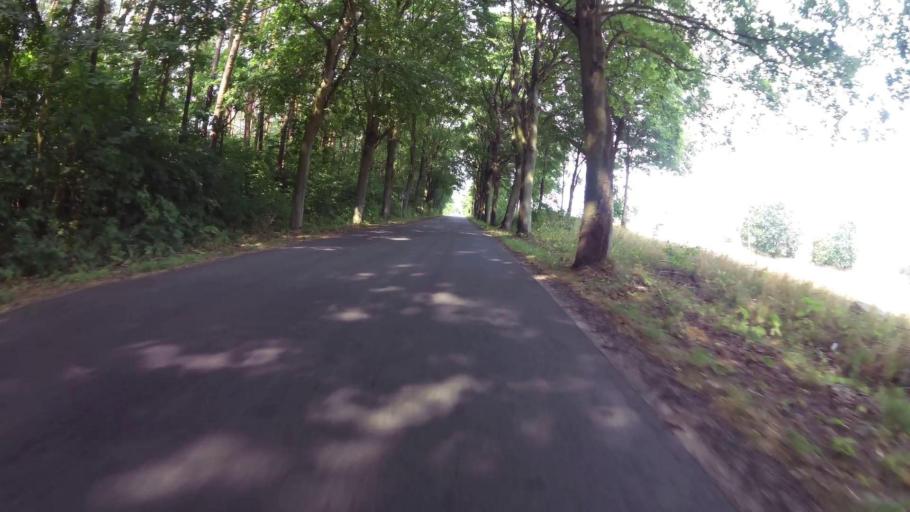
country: PL
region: West Pomeranian Voivodeship
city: Trzcinsko Zdroj
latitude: 52.9363
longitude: 14.6559
